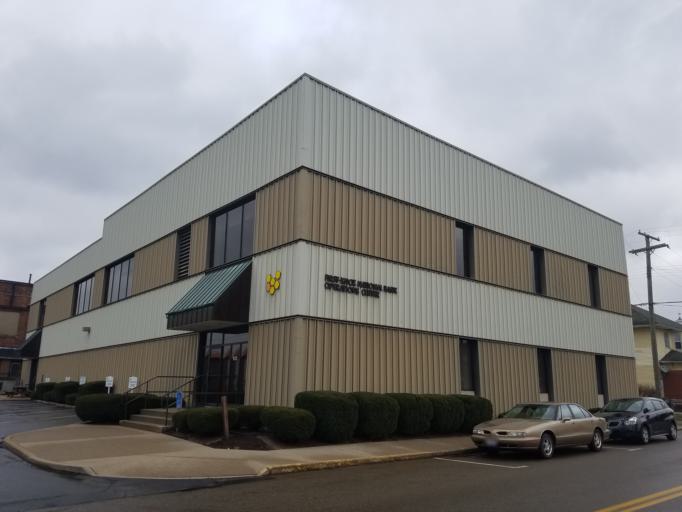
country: US
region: Ohio
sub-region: Knox County
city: Mount Vernon
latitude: 40.3927
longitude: -82.4887
